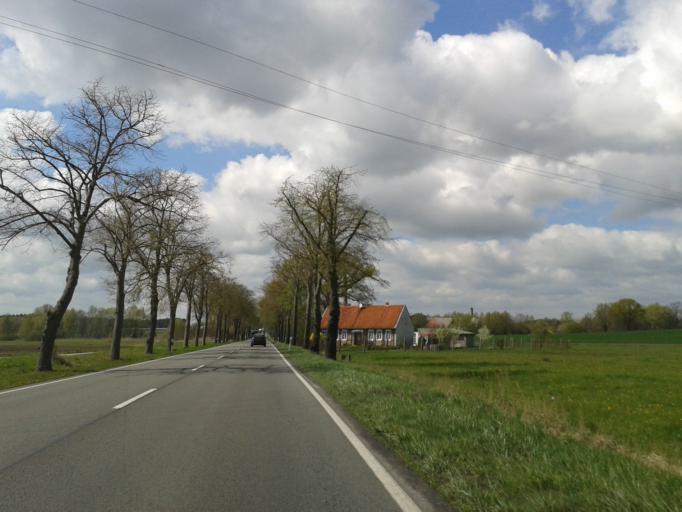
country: DE
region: Saxony-Anhalt
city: Salzwedel
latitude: 52.8623
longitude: 11.1134
